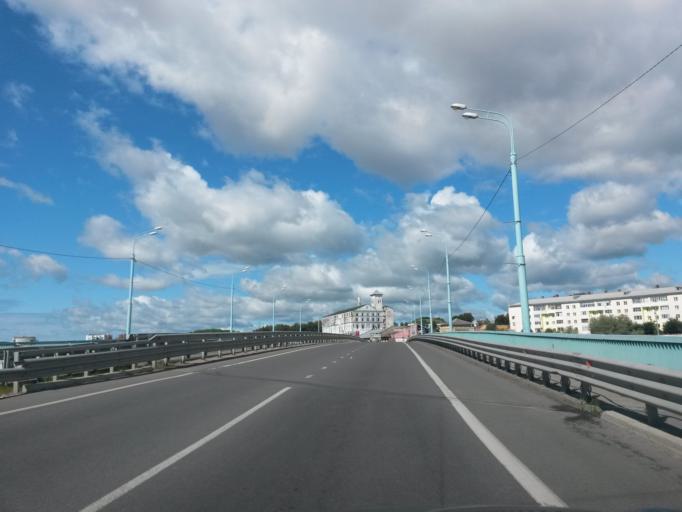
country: RU
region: Jaroslavl
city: Yaroslavl
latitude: 57.6189
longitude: 39.8839
